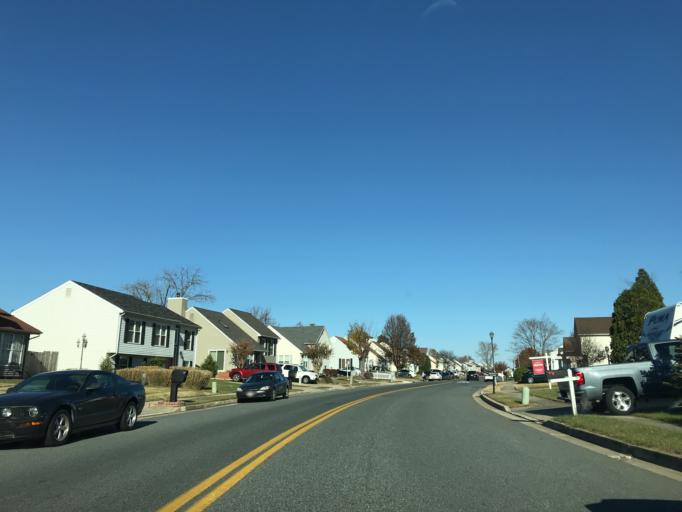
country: US
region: Maryland
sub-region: Baltimore County
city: Bowleys Quarters
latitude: 39.3633
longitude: -76.3609
